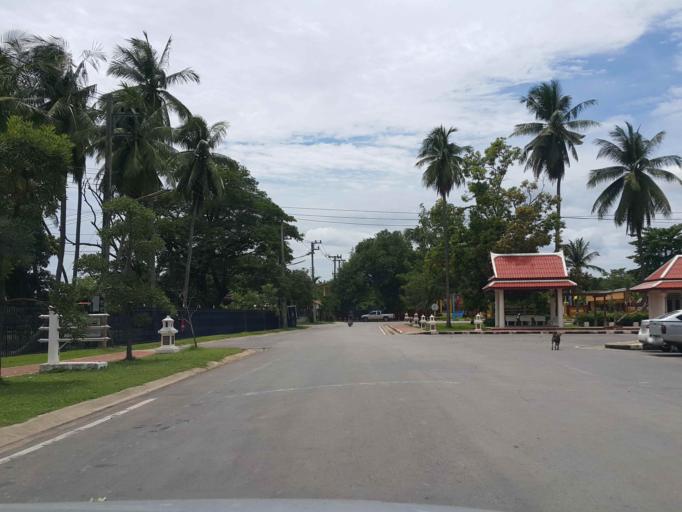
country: TH
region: Sukhothai
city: Ban Na
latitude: 17.0172
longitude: 99.7069
